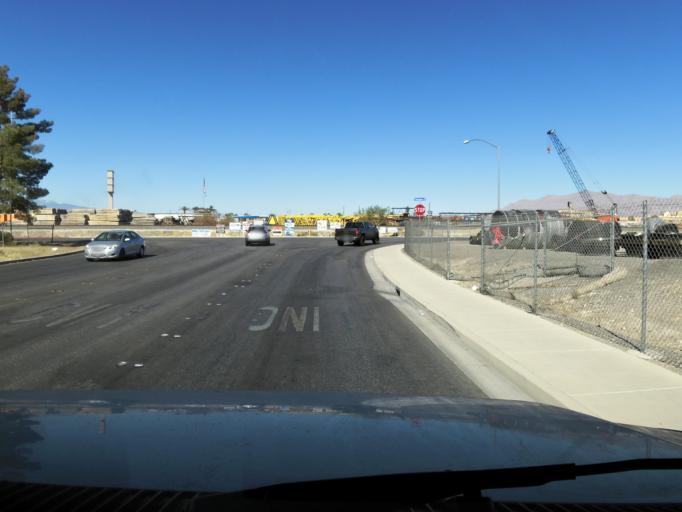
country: US
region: Nevada
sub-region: Clark County
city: North Las Vegas
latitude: 36.2373
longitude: -115.1085
